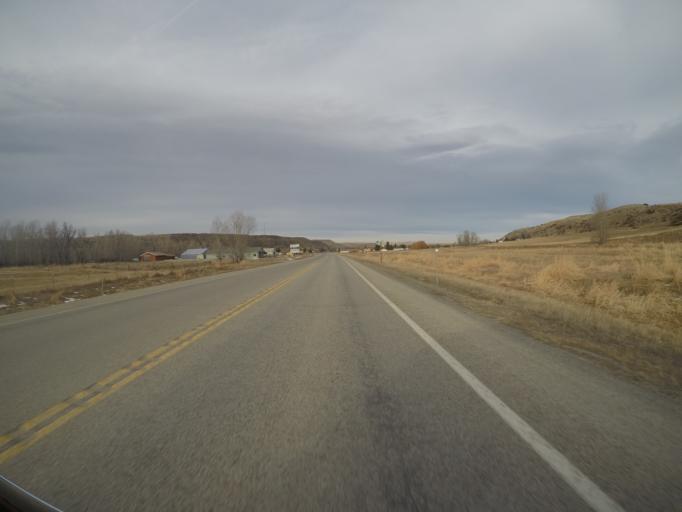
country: US
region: Montana
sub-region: Stillwater County
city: Absarokee
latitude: 45.5073
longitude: -109.4486
